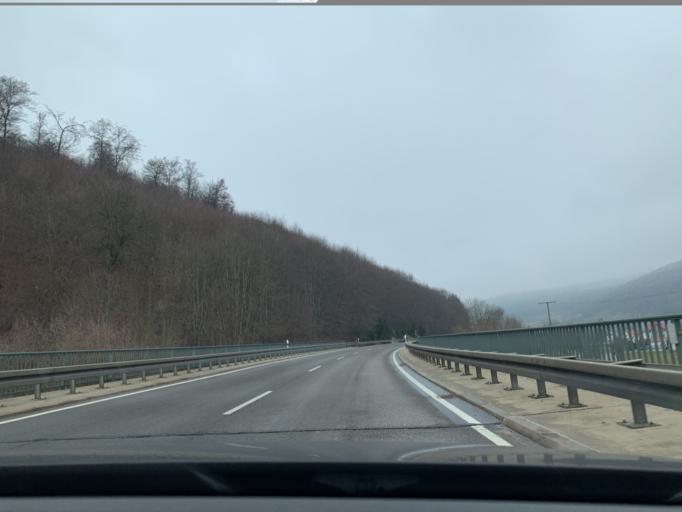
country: DE
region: Baden-Wuerttemberg
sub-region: Freiburg Region
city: Geisingen
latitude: 47.9127
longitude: 8.6745
